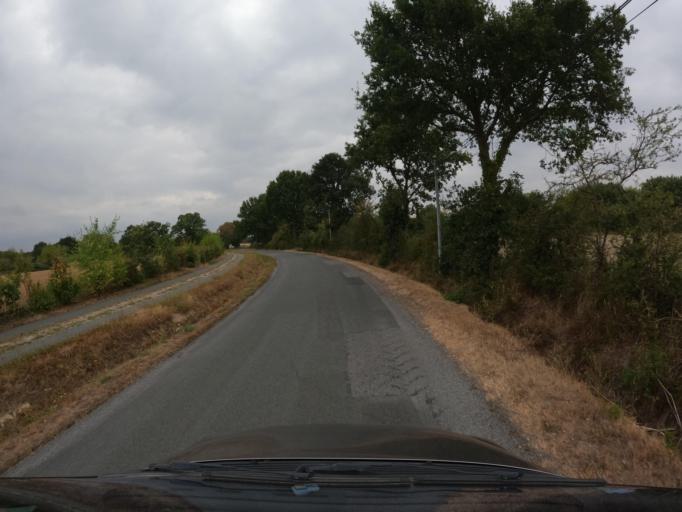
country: FR
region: Pays de la Loire
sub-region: Departement de la Vendee
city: La Guyonniere
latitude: 46.9671
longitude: -1.2676
